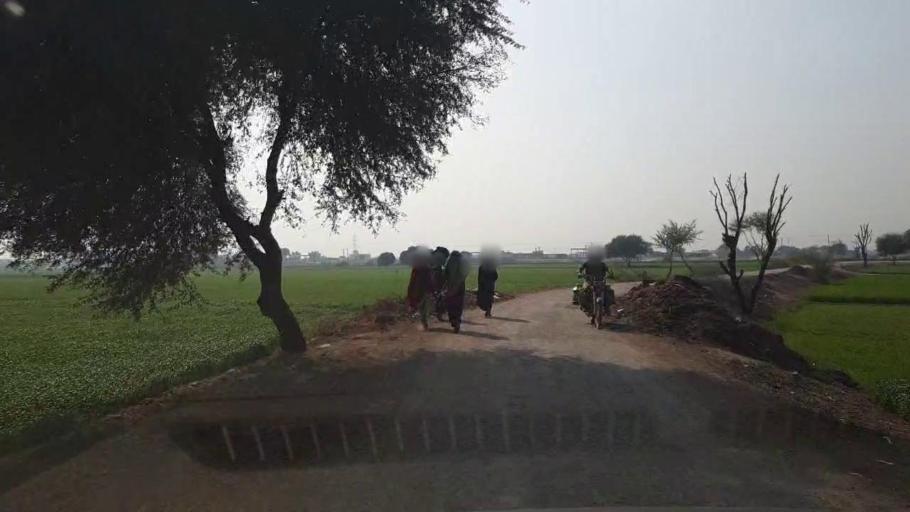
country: PK
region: Sindh
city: Hala
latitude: 25.8441
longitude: 68.4217
